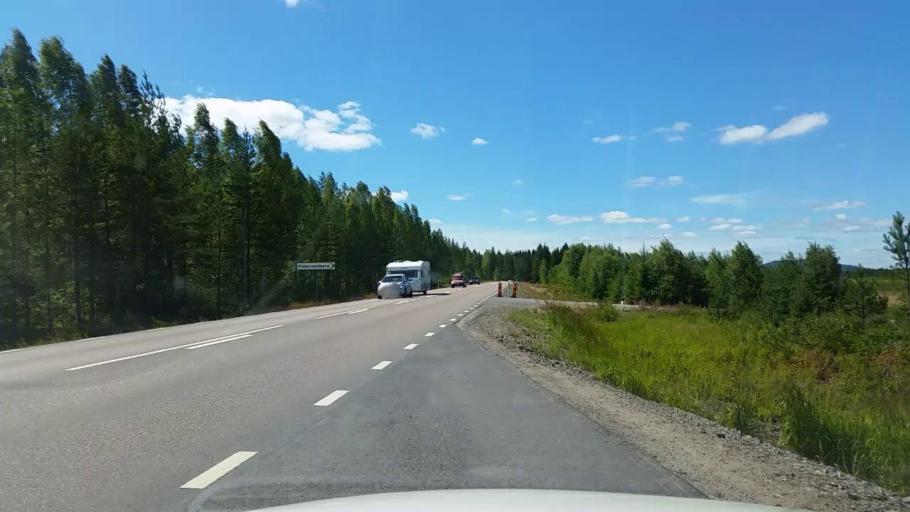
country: SE
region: Gaevleborg
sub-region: Ljusdals Kommun
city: Ljusdal
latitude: 61.8173
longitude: 16.0168
